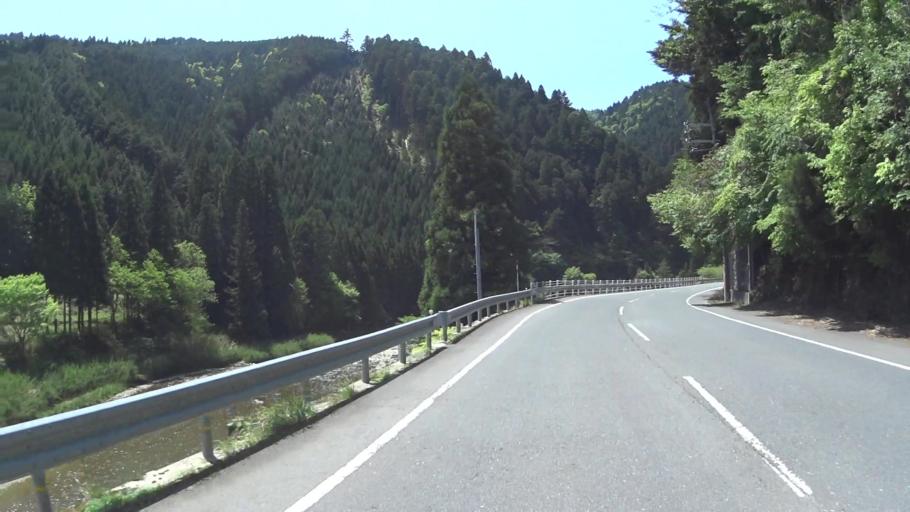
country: JP
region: Shiga Prefecture
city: Kitahama
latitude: 35.2041
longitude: 135.7656
